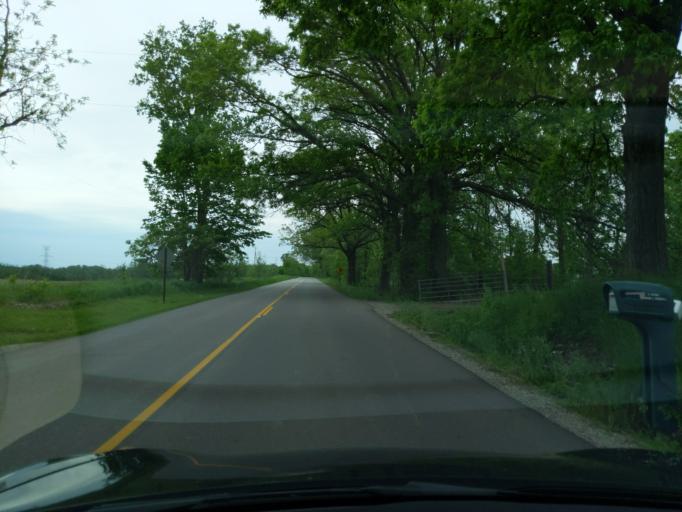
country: US
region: Michigan
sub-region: Ingham County
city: Leslie
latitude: 42.4142
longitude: -84.3540
